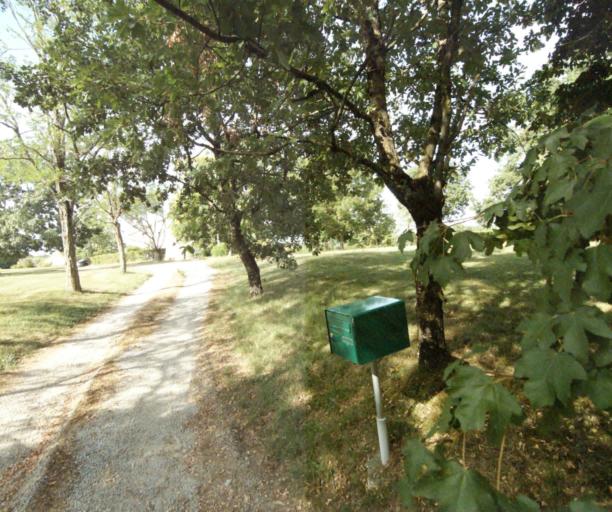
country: FR
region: Midi-Pyrenees
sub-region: Departement du Tarn
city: Soual
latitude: 43.5357
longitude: 2.0743
